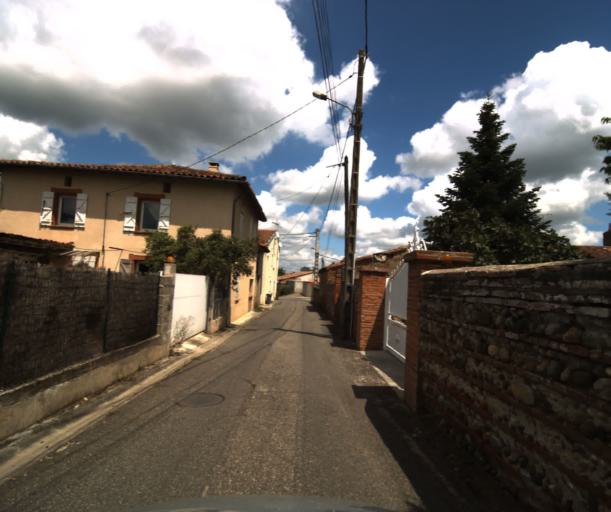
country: FR
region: Midi-Pyrenees
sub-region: Departement de la Haute-Garonne
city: Lacasse
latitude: 43.3988
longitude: 1.2694
